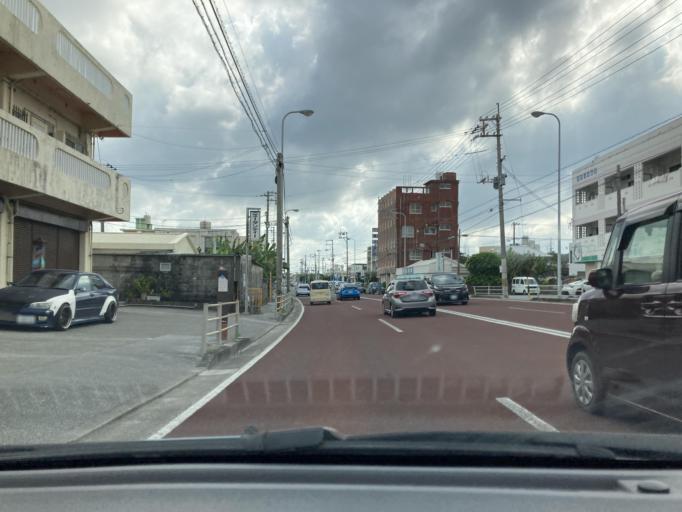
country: JP
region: Okinawa
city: Ginowan
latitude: 26.2144
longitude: 127.7620
